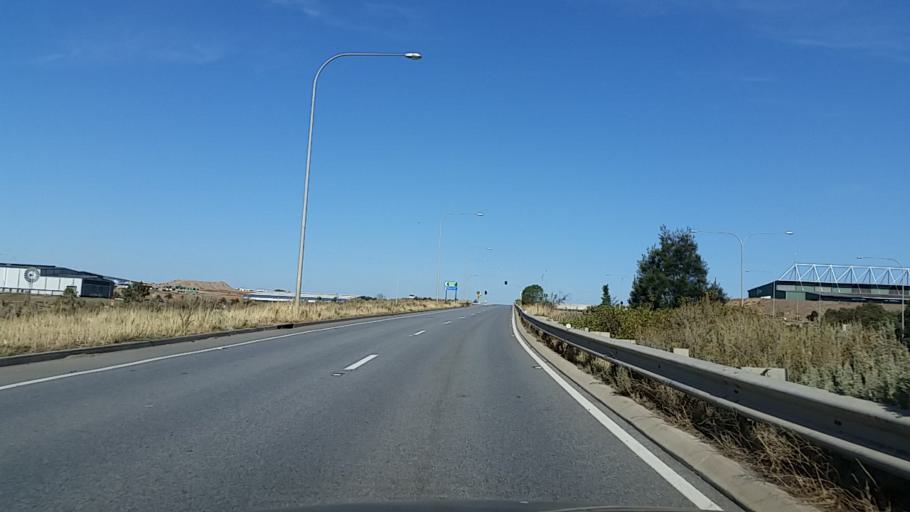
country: AU
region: South Australia
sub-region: Port Adelaide Enfield
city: Alberton
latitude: -34.8336
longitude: 138.5426
